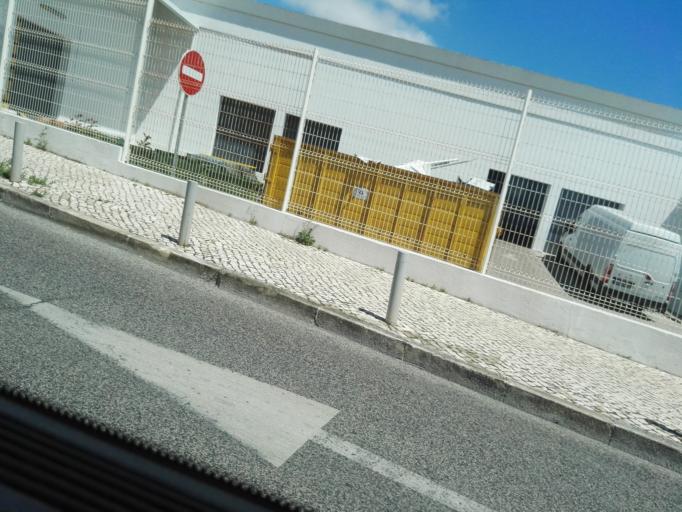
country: PT
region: Lisbon
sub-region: Oeiras
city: Linda-a-Velha
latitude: 38.7177
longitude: -9.2386
